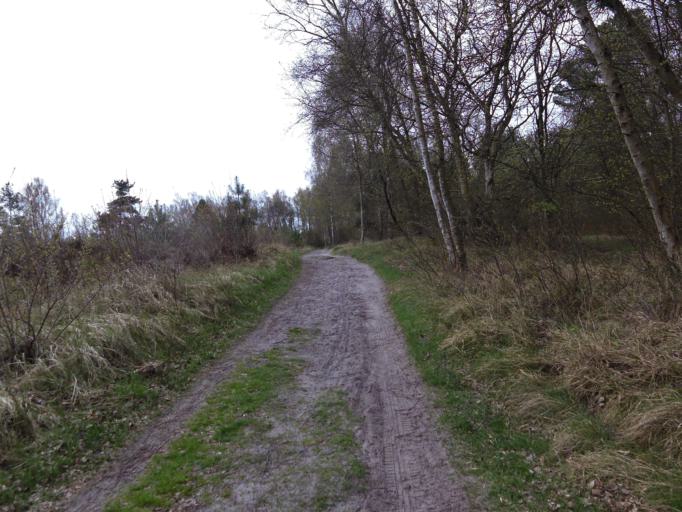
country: DE
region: Mecklenburg-Vorpommern
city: Hiddensee
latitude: 54.5375
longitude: 13.0896
